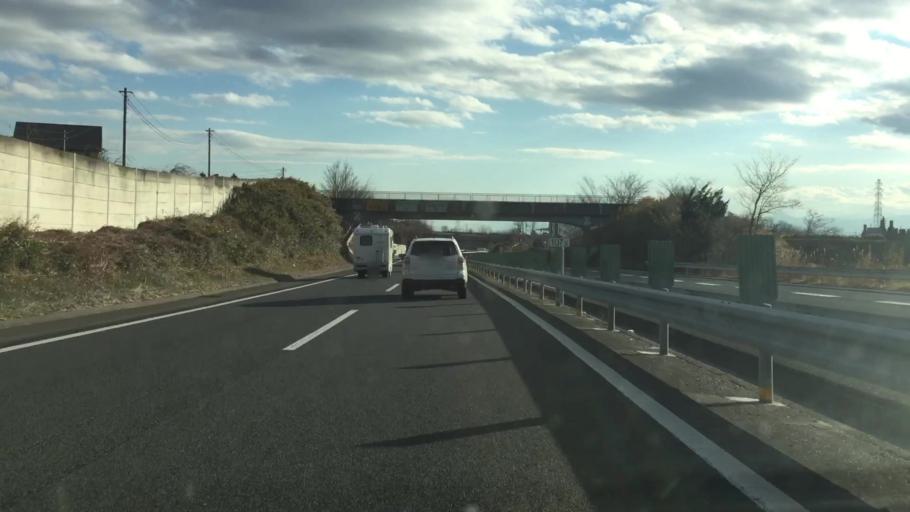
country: JP
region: Gunma
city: Shibukawa
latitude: 36.5085
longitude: 139.0318
